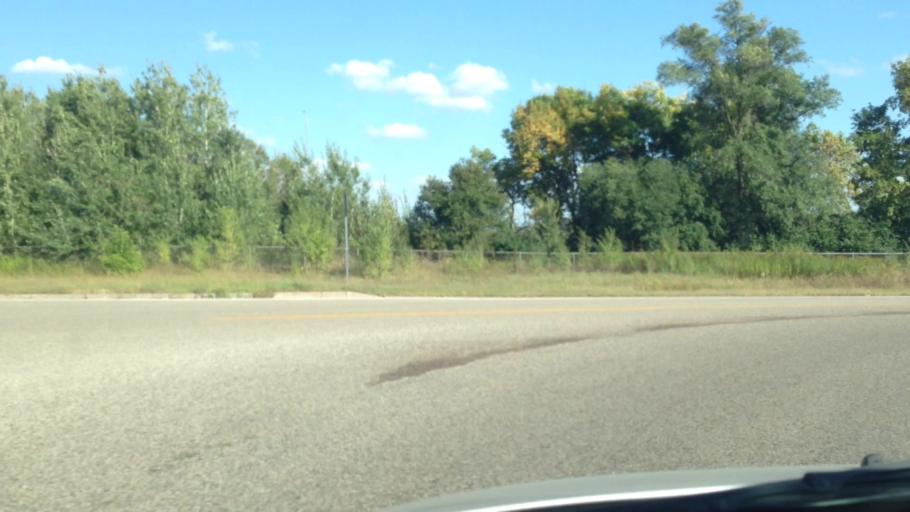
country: US
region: Minnesota
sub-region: Ramsey County
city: Mounds View
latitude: 45.1267
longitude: -93.1908
